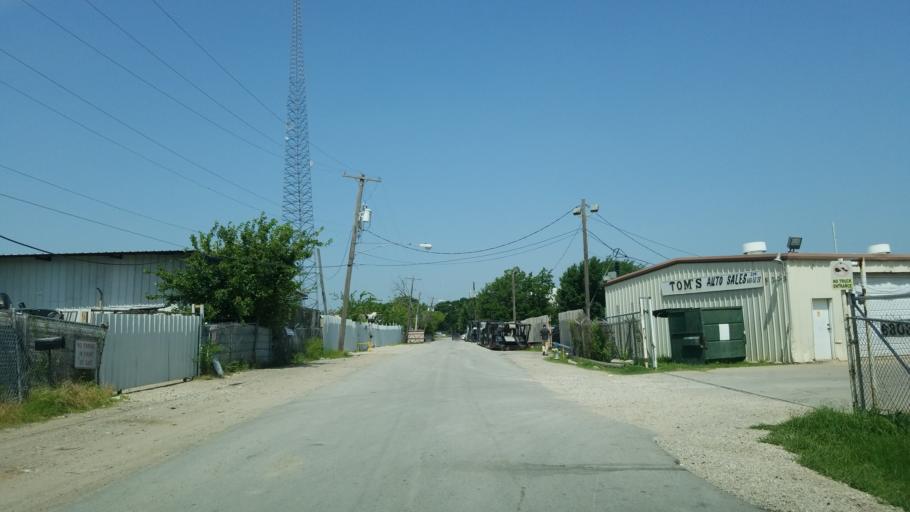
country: US
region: Texas
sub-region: Dallas County
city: Irving
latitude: 32.7792
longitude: -96.9208
